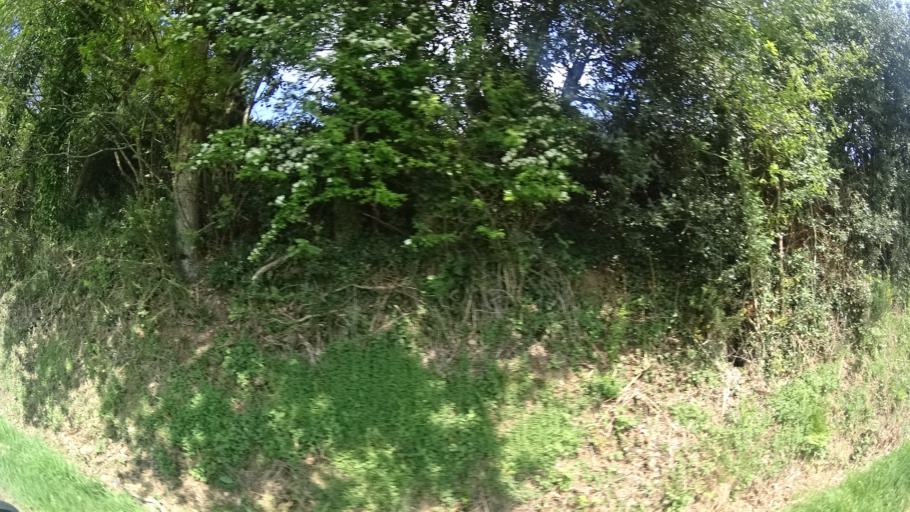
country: FR
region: Brittany
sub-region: Departement du Morbihan
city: Beganne
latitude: 47.5804
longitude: -2.2837
